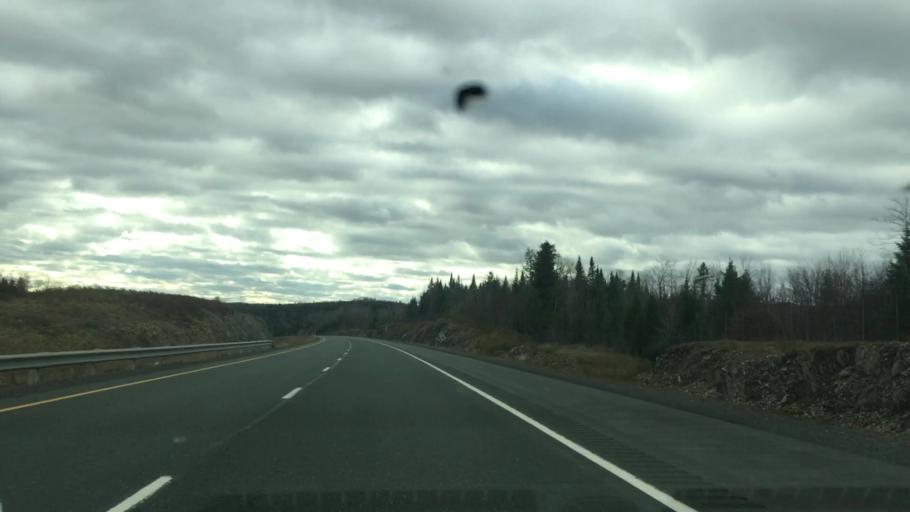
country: US
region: Maine
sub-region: Aroostook County
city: Easton
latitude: 46.6046
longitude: -67.7448
